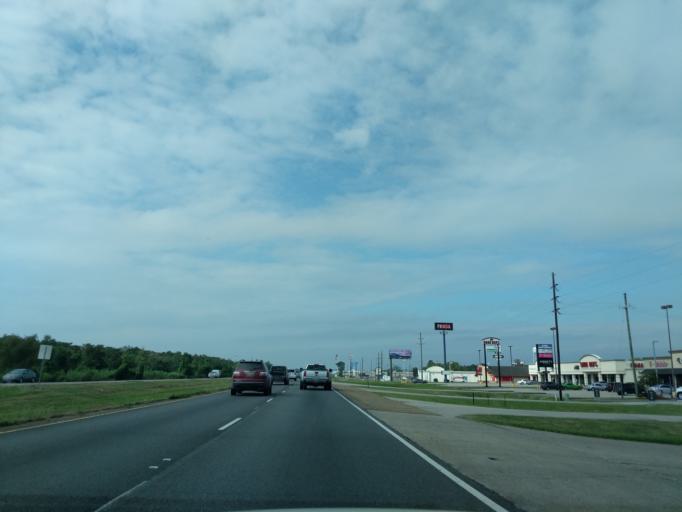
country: US
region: Louisiana
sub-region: Saint Mary Parish
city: Bayou Vista
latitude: 29.6828
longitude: -91.2618
